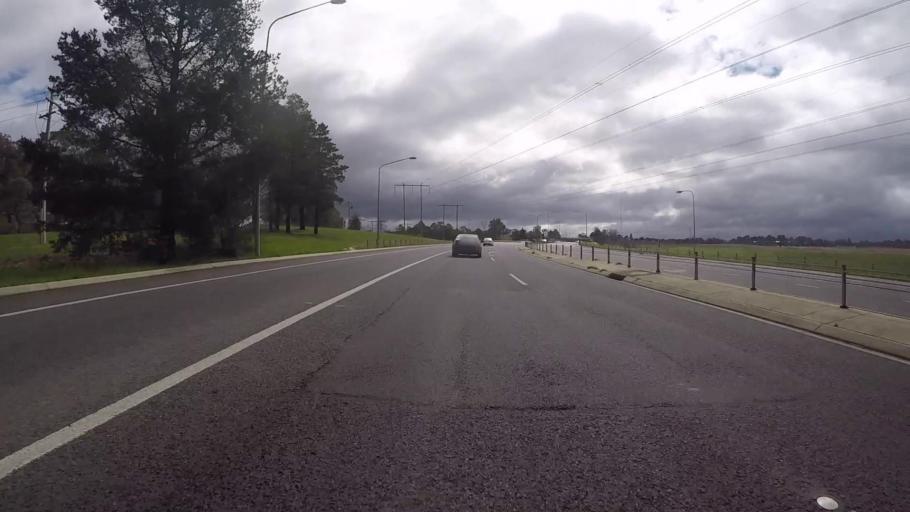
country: AU
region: Australian Capital Territory
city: Kaleen
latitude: -35.2322
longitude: 149.1253
